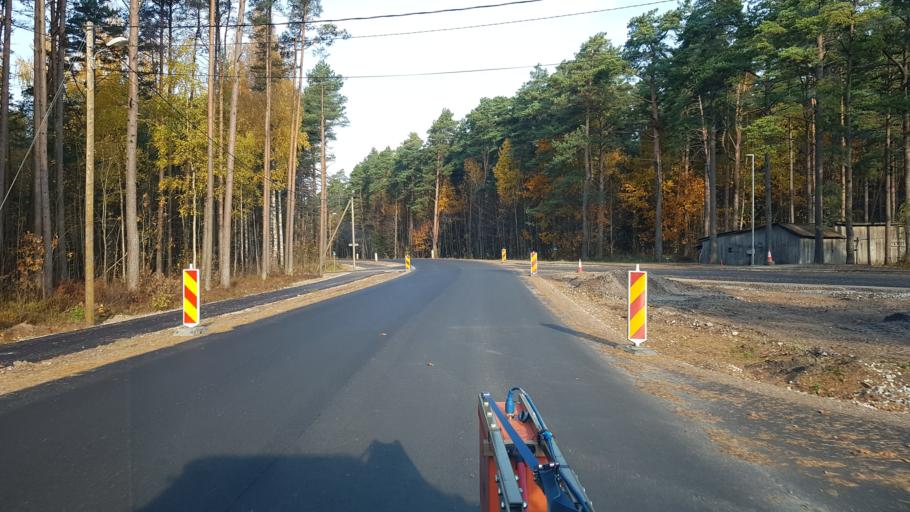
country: EE
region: Paernumaa
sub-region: Paikuse vald
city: Paikuse
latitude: 58.3626
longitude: 24.6062
